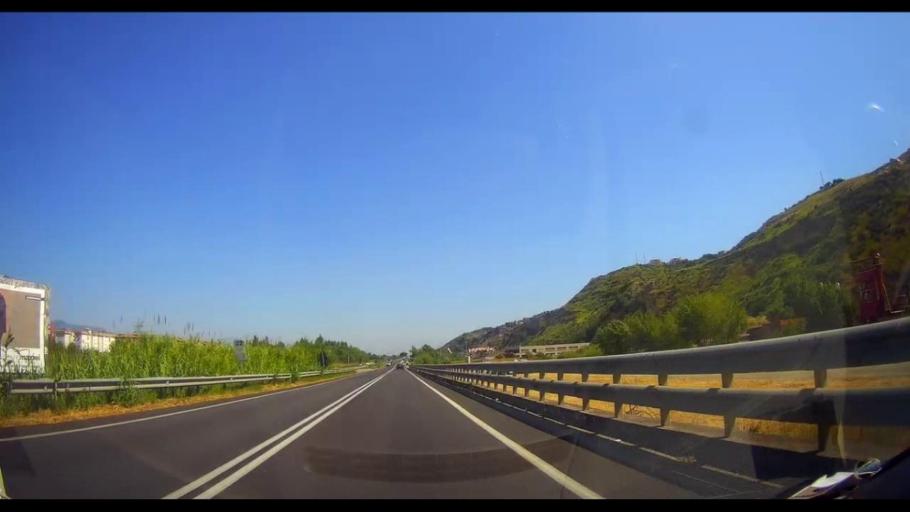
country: IT
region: Calabria
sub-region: Provincia di Cosenza
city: Cosenza
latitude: 39.3024
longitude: 16.2648
